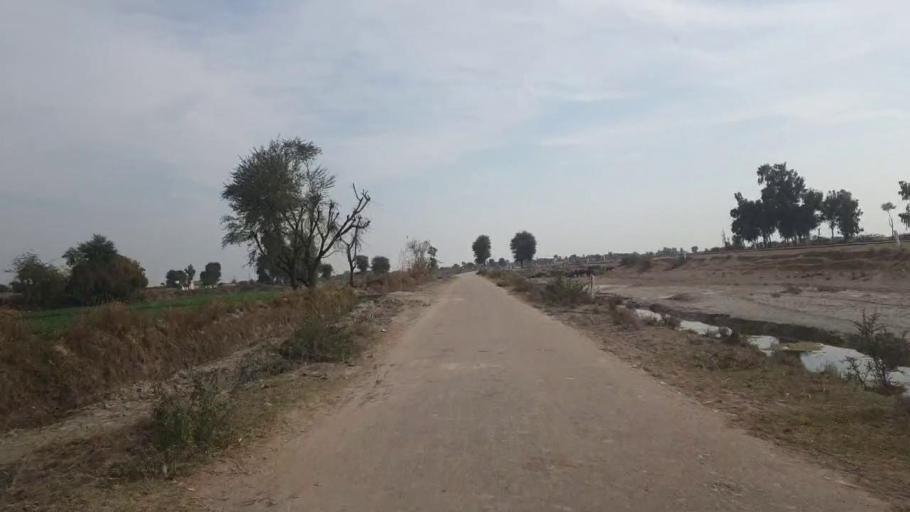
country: PK
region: Sindh
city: Nawabshah
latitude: 26.0882
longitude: 68.4861
